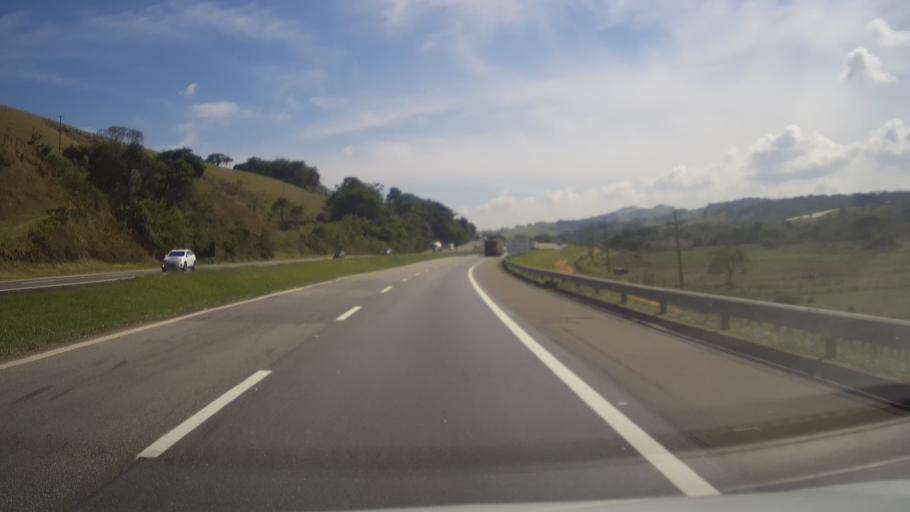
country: BR
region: Minas Gerais
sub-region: Cambui
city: Cambui
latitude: -22.5809
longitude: -46.0452
